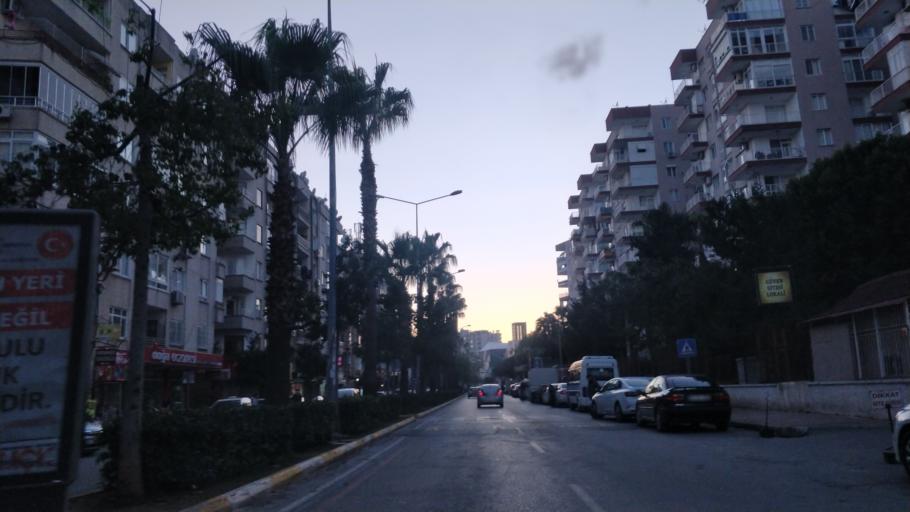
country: TR
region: Mersin
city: Mercin
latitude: 36.7860
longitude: 34.5928
